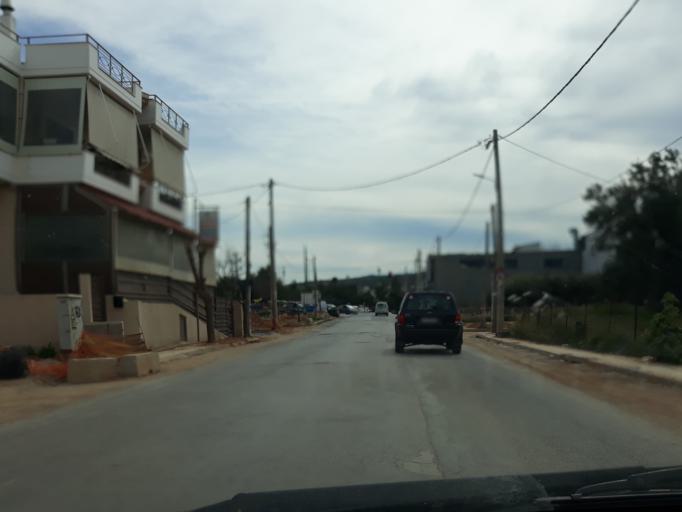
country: GR
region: Attica
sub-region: Nomarchia Dytikis Attikis
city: Ano Liosia
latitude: 38.0809
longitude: 23.7102
